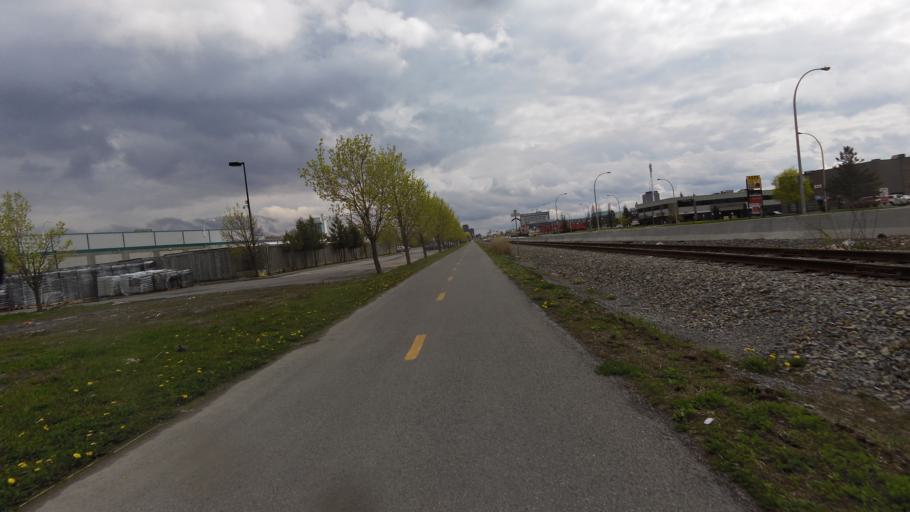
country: CA
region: Quebec
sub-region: Outaouais
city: Gatineau
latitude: 45.4548
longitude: -75.7298
